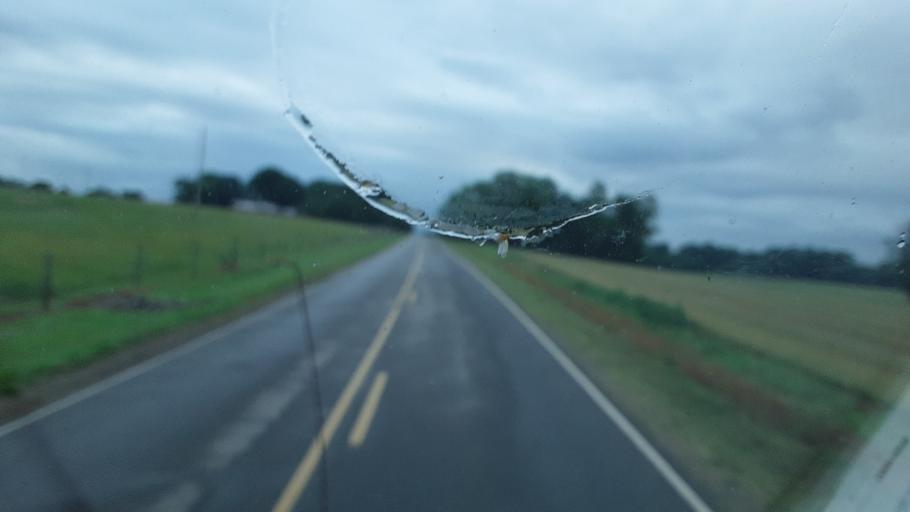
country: US
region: North Carolina
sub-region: Yadkin County
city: Jonesville
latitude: 36.0614
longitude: -80.8315
